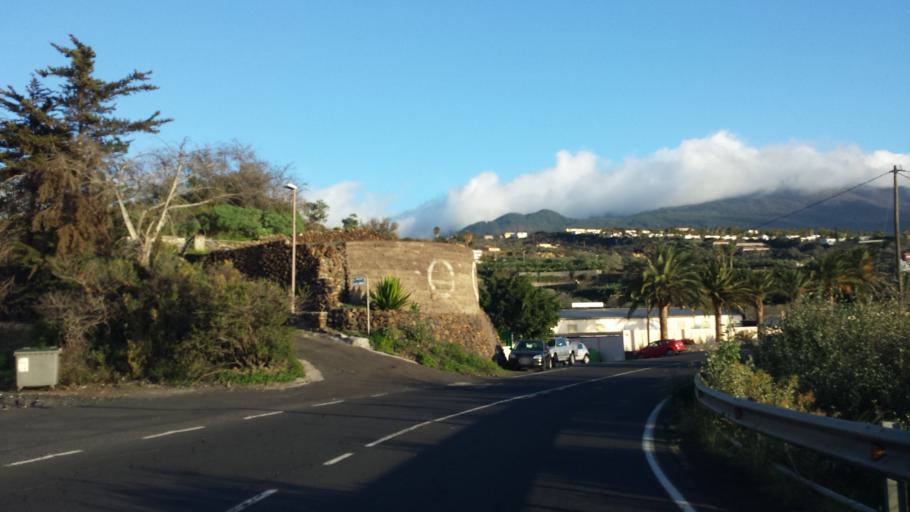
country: ES
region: Canary Islands
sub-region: Provincia de Santa Cruz de Tenerife
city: Los Llanos de Aridane
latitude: 28.6539
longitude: -17.9028
